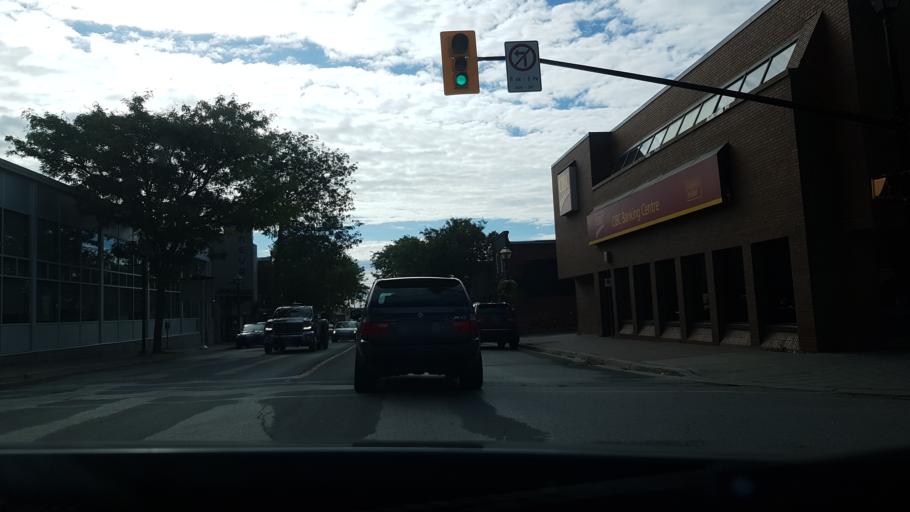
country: CA
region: Ontario
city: Orillia
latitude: 44.6083
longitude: -79.4198
